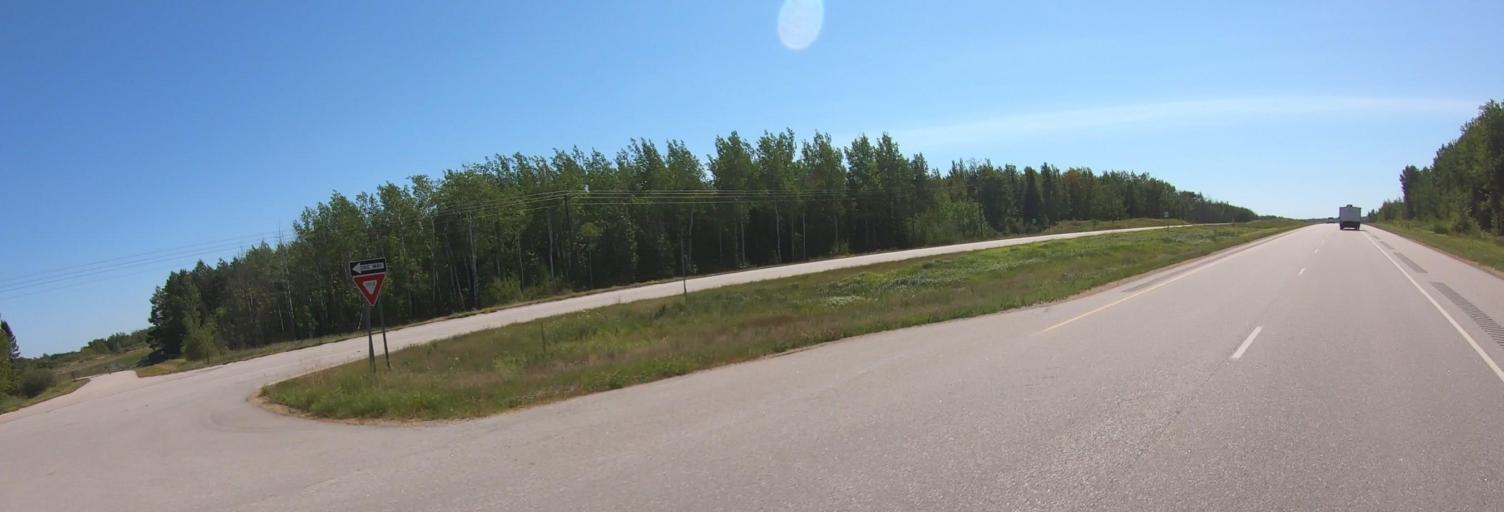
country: US
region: Minnesota
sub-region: Saint Louis County
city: Mountain Iron
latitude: 47.7927
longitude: -92.6652
